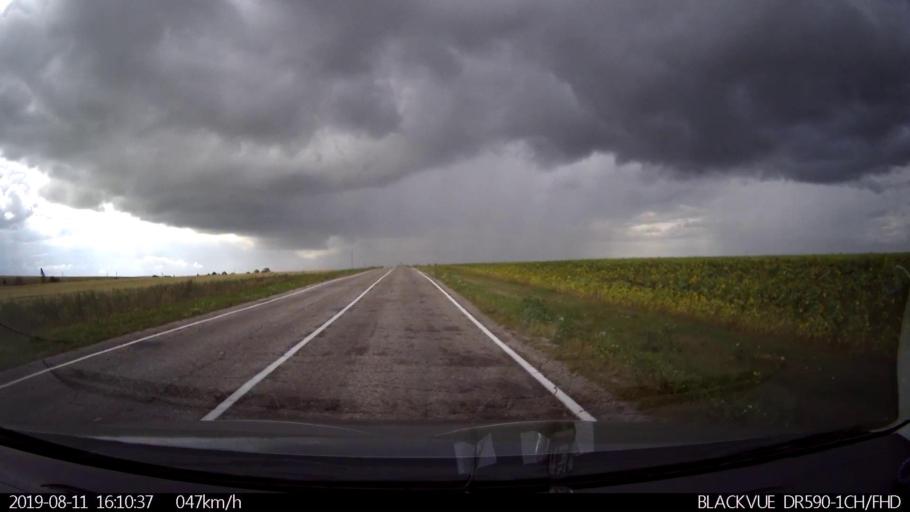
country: RU
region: Ulyanovsk
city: Ignatovka
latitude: 53.9994
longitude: 47.6534
